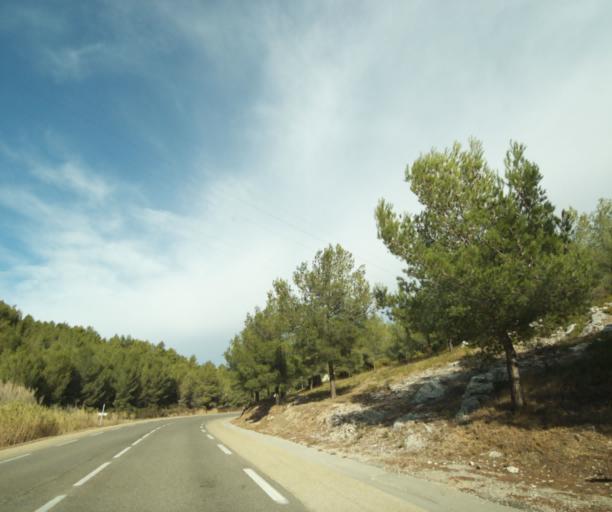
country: FR
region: Provence-Alpes-Cote d'Azur
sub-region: Departement des Bouches-du-Rhone
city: Sausset-les-Pins
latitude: 43.3504
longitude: 5.1015
